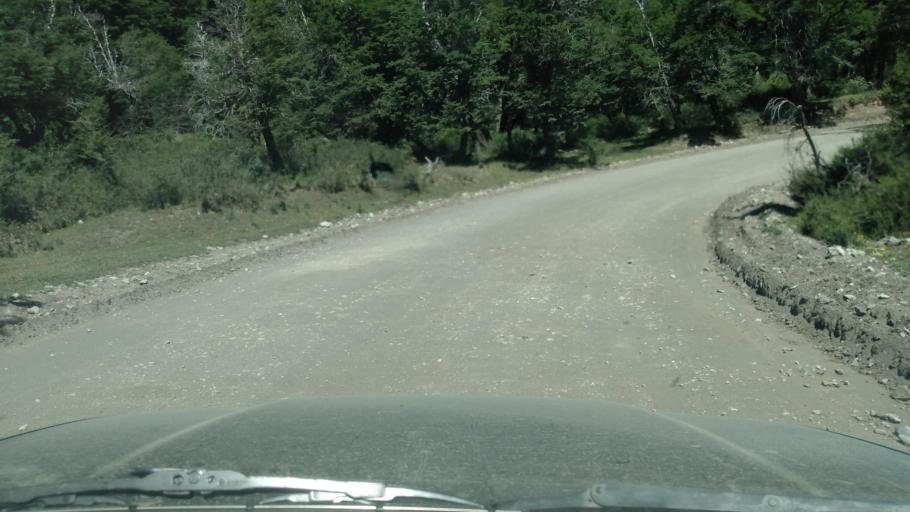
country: AR
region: Neuquen
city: Villa La Angostura
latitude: -40.6217
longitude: -71.5790
